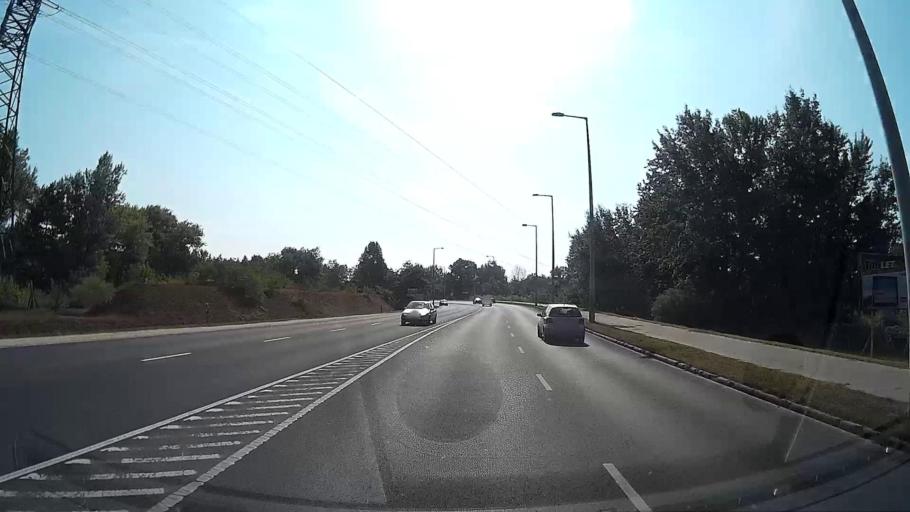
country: HU
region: Budapest
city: Budapest IV. keruelet
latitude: 47.5956
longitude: 19.0918
